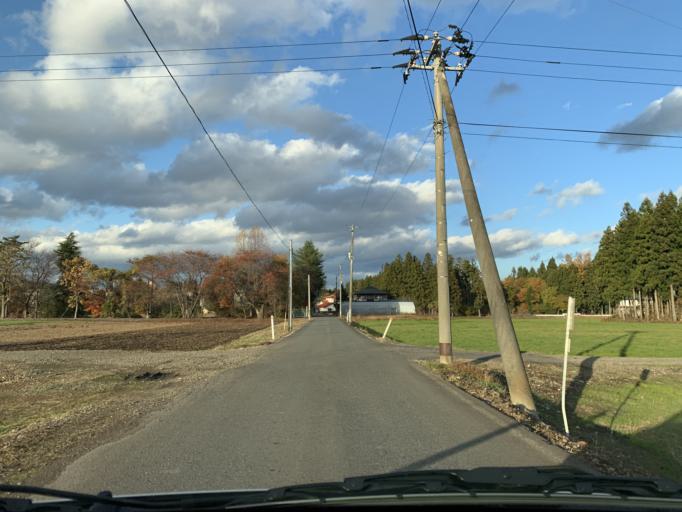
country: JP
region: Iwate
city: Mizusawa
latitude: 39.1260
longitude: 141.0302
